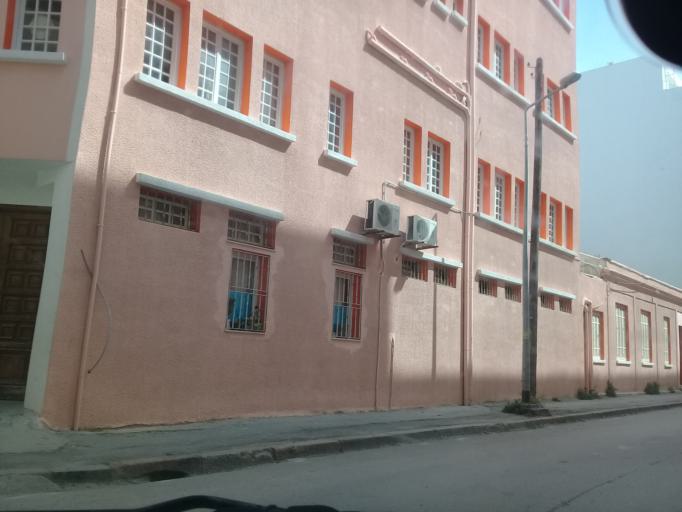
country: TN
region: Tunis
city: Tunis
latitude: 36.8198
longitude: 10.1806
